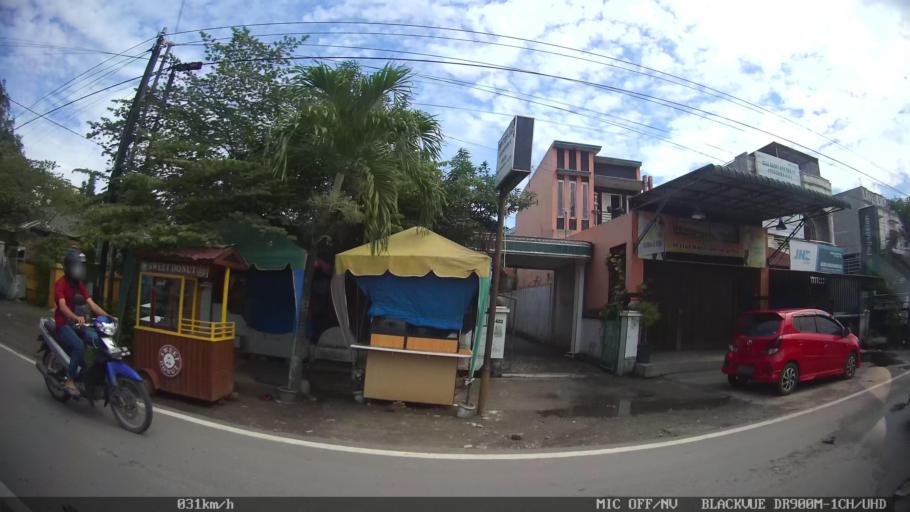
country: ID
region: North Sumatra
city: Medan
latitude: 3.6222
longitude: 98.7050
